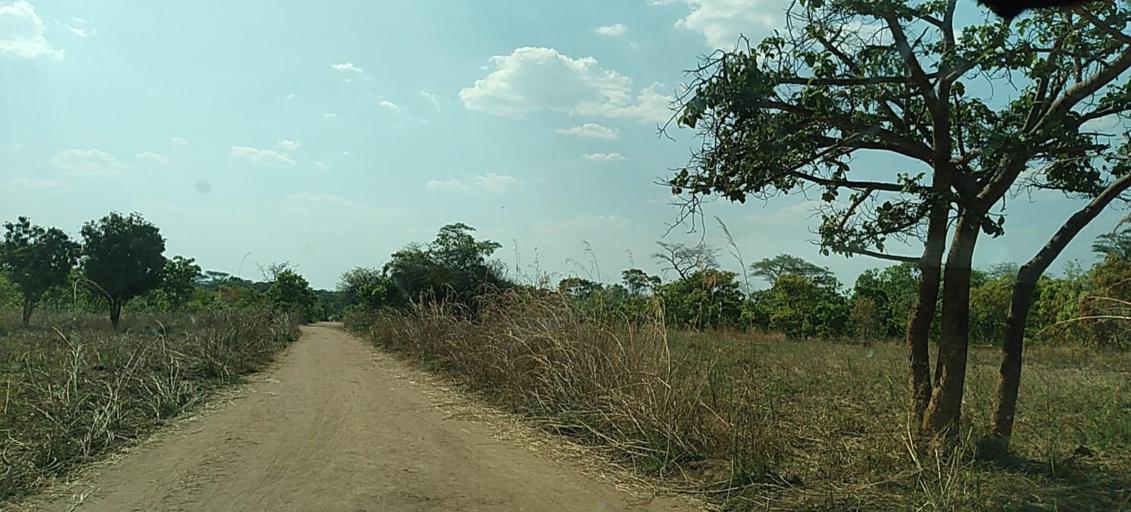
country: ZM
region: North-Western
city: Kalengwa
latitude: -13.1080
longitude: 24.9925
